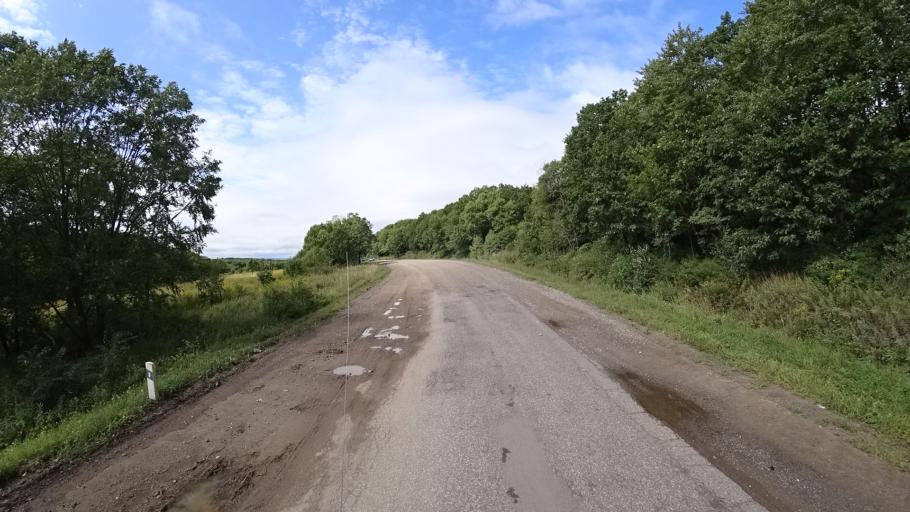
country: RU
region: Primorskiy
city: Lyalichi
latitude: 44.1472
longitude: 132.3985
